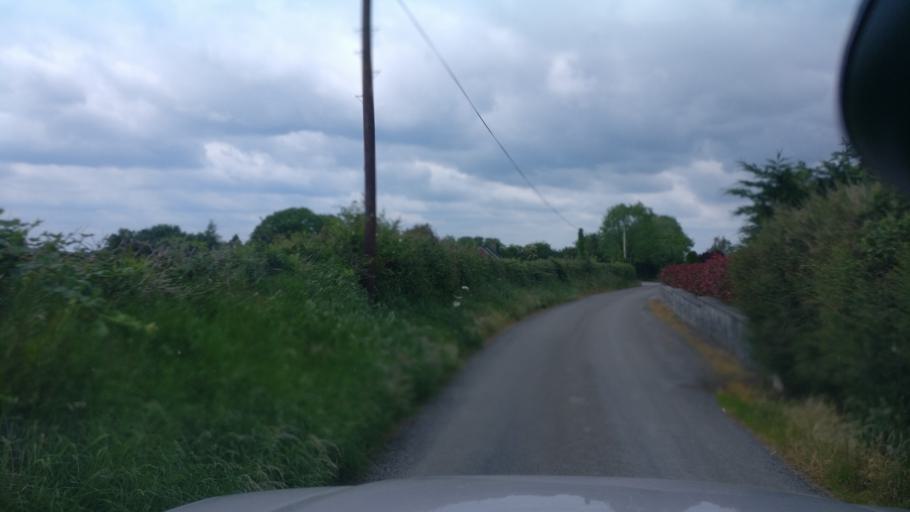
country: IE
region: Connaught
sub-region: County Galway
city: Ballinasloe
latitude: 53.2977
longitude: -8.3179
